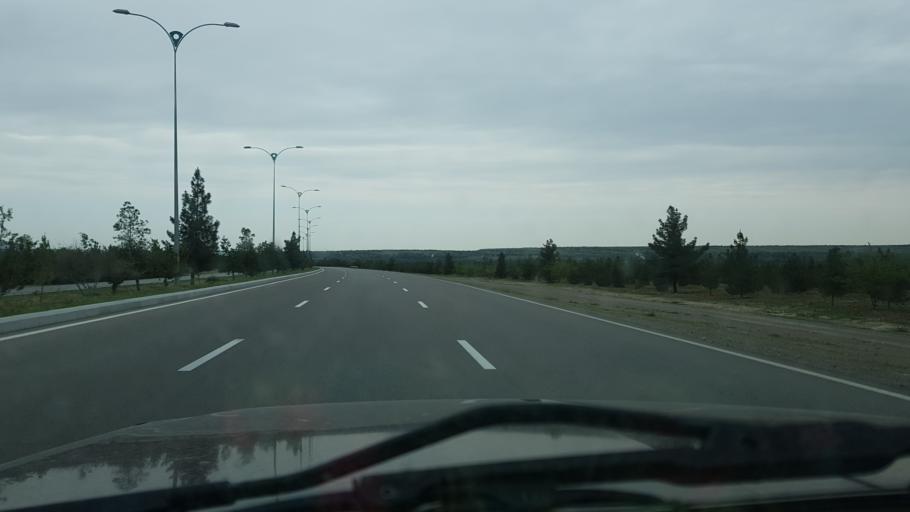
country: TM
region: Ahal
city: Abadan
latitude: 37.9237
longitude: 58.2460
